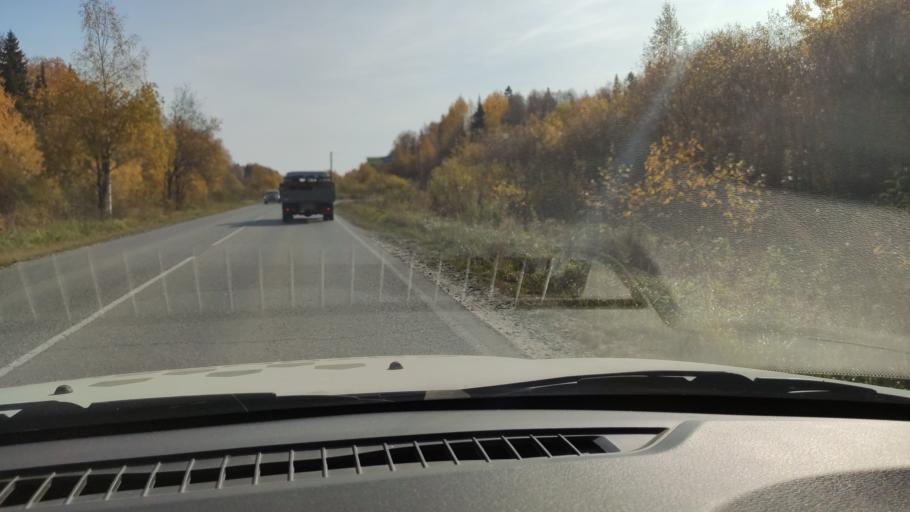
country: RU
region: Perm
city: Novyye Lyady
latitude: 58.0331
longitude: 56.6106
